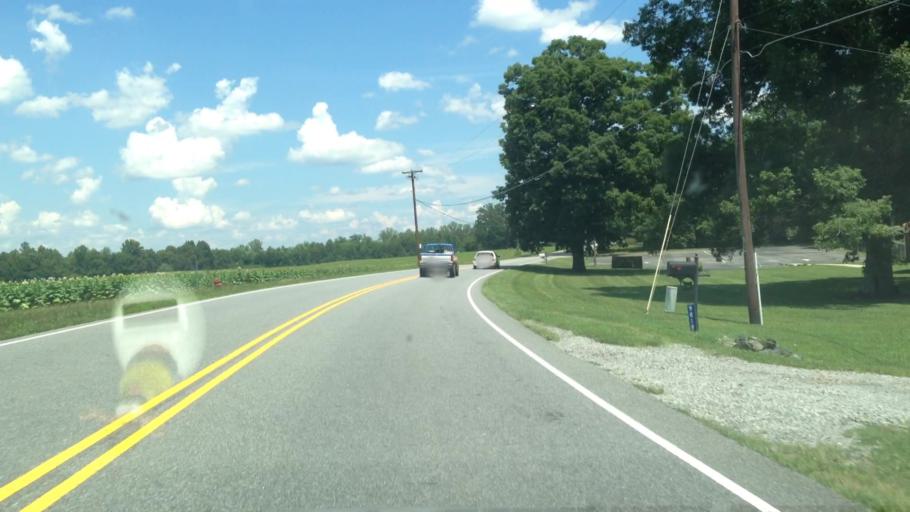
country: US
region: North Carolina
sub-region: Rockingham County
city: Reidsville
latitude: 36.2877
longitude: -79.7496
